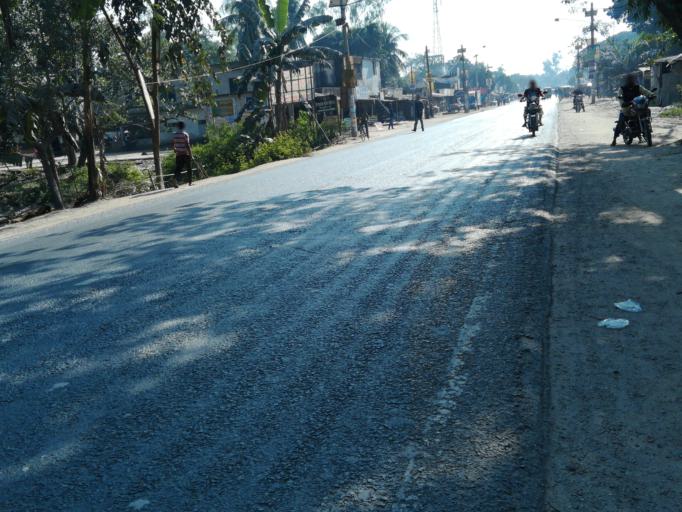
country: BD
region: Rangpur Division
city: Rangpur
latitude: 25.5731
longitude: 89.2744
